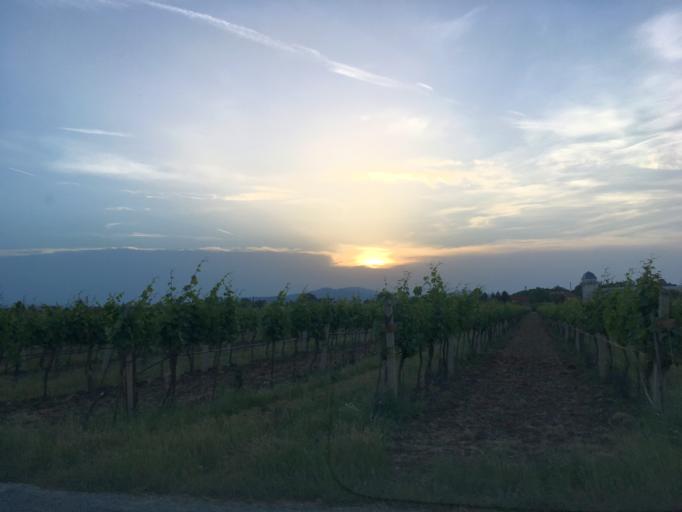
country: AT
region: Lower Austria
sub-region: Politischer Bezirk Baden
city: Teesdorf
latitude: 47.9470
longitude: 16.2911
